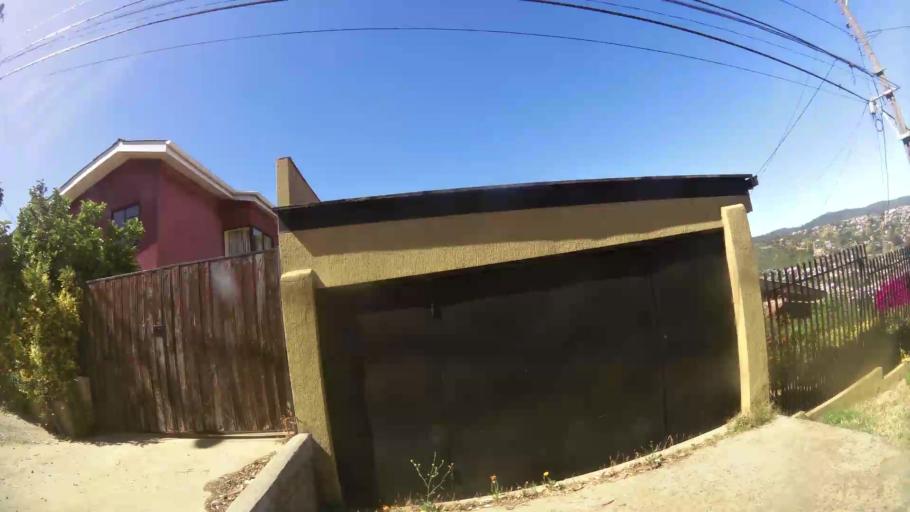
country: CL
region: Valparaiso
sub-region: Provincia de Valparaiso
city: Vina del Mar
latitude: -33.0651
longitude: -71.5787
